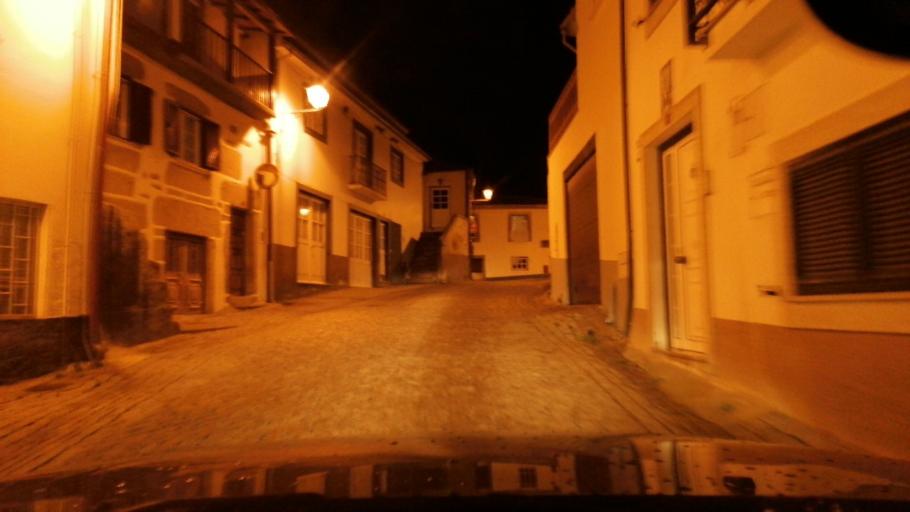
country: PT
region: Viseu
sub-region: Sao Joao da Pesqueira
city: Sao Joao da Pesqueira
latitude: 41.0812
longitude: -7.4353
